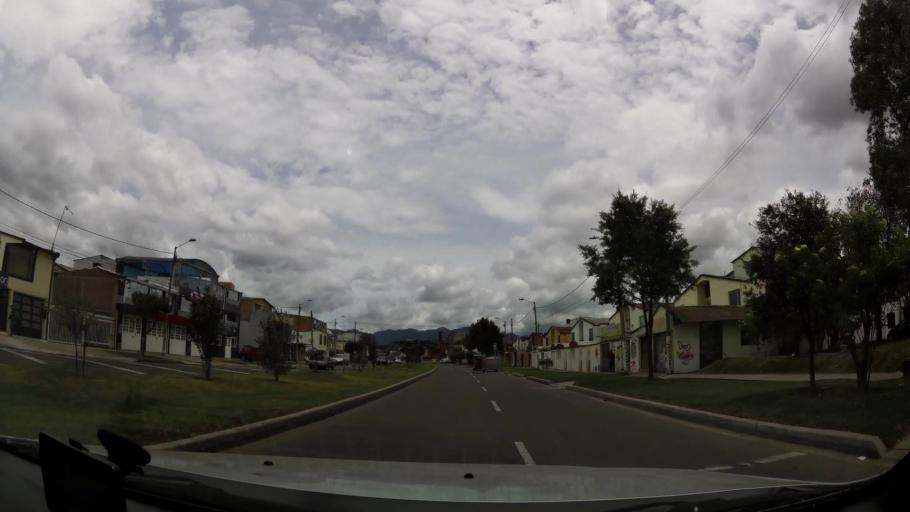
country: CO
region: Bogota D.C.
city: Bogota
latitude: 4.6392
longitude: -74.1436
